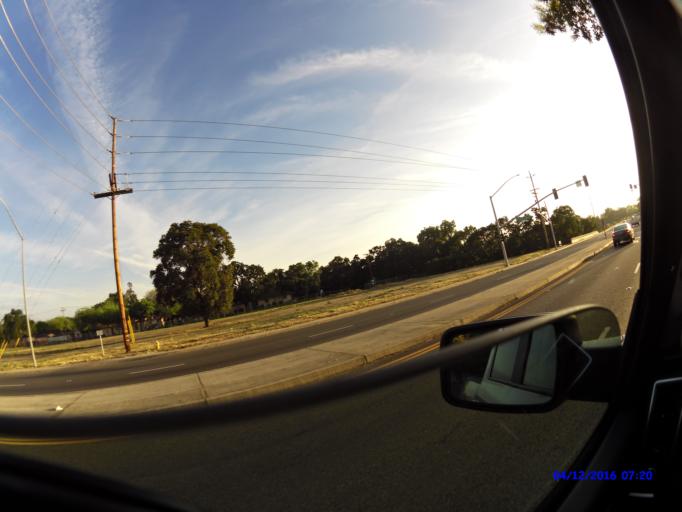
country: US
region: California
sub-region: Stanislaus County
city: Modesto
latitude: 37.6374
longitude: -120.9854
